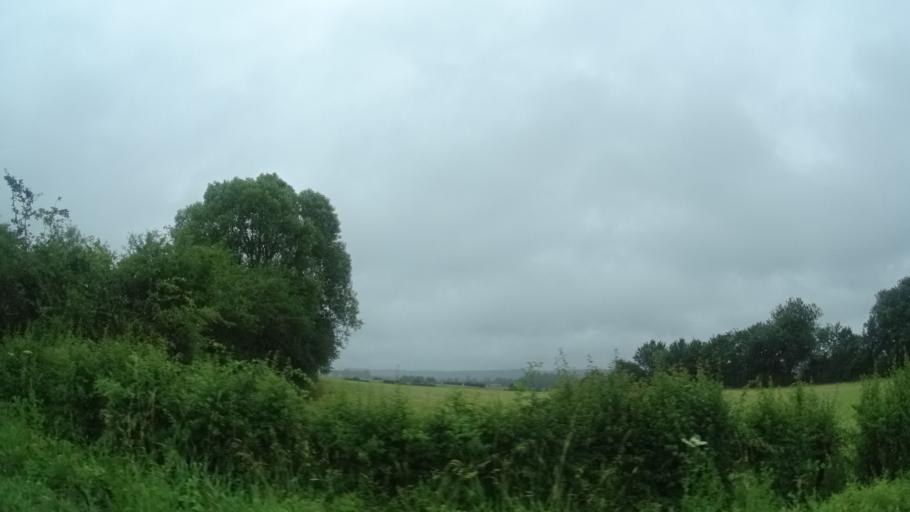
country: BE
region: Wallonia
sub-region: Province du Luxembourg
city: Habay-la-Vieille
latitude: 49.6802
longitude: 5.6635
